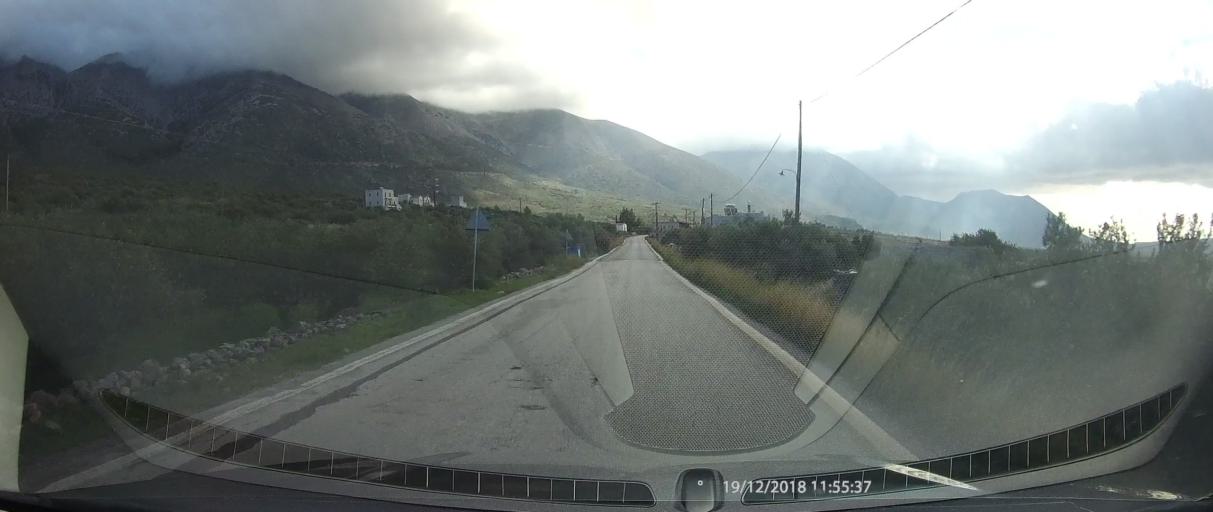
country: GR
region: Peloponnese
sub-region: Nomos Lakonias
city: Gytheio
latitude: 36.6069
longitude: 22.3949
